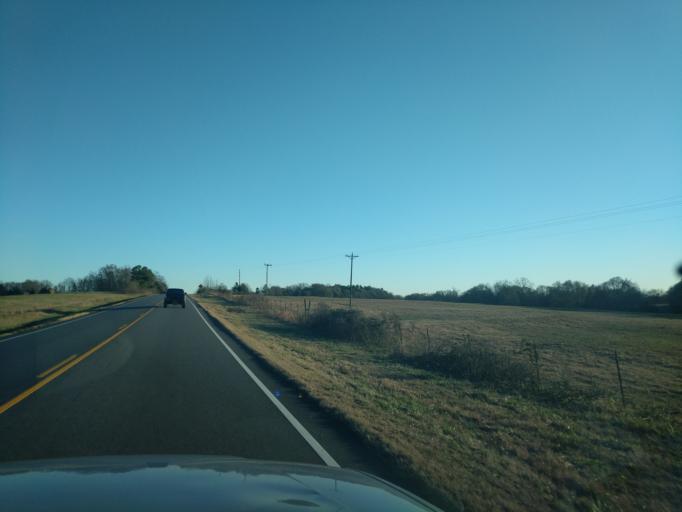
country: US
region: South Carolina
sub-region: Oconee County
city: Utica
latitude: 34.5789
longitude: -82.9137
